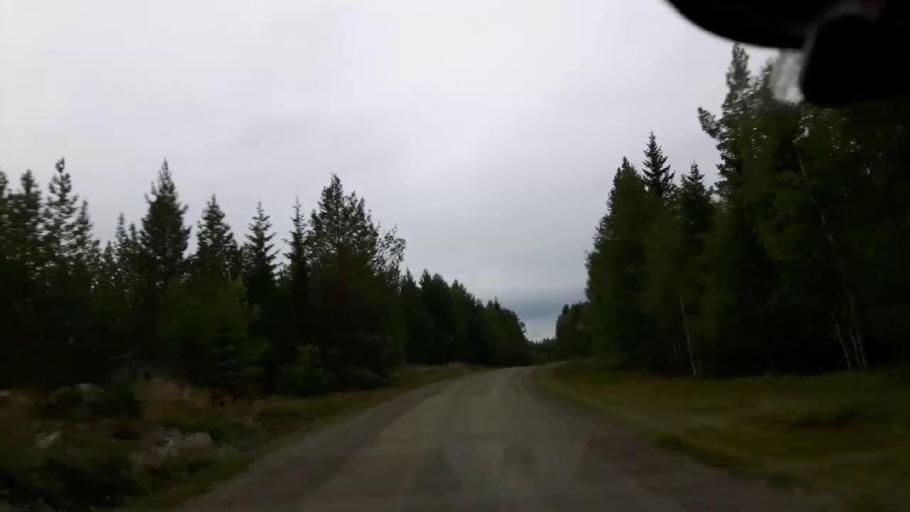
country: SE
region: Vaesternorrland
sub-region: Ange Kommun
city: Fransta
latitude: 62.8571
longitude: 15.9808
